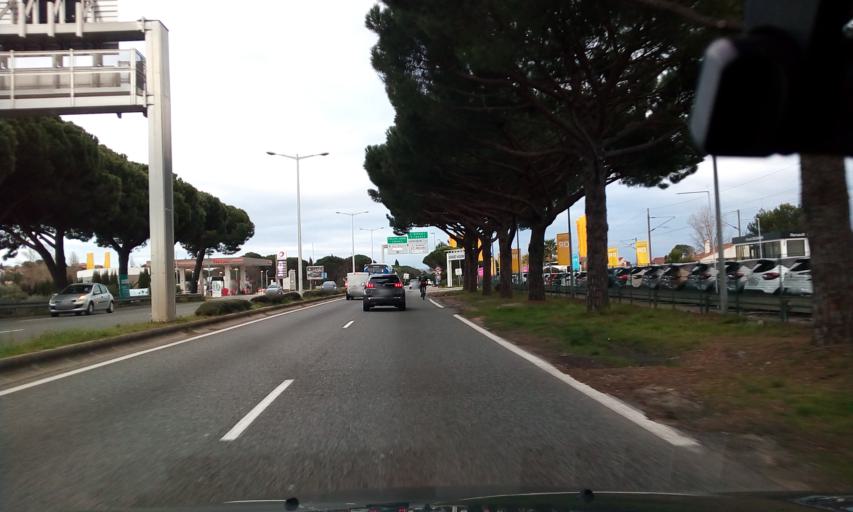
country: FR
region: Provence-Alpes-Cote d'Azur
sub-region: Departement du Var
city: Frejus
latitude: 43.4358
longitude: 6.7236
